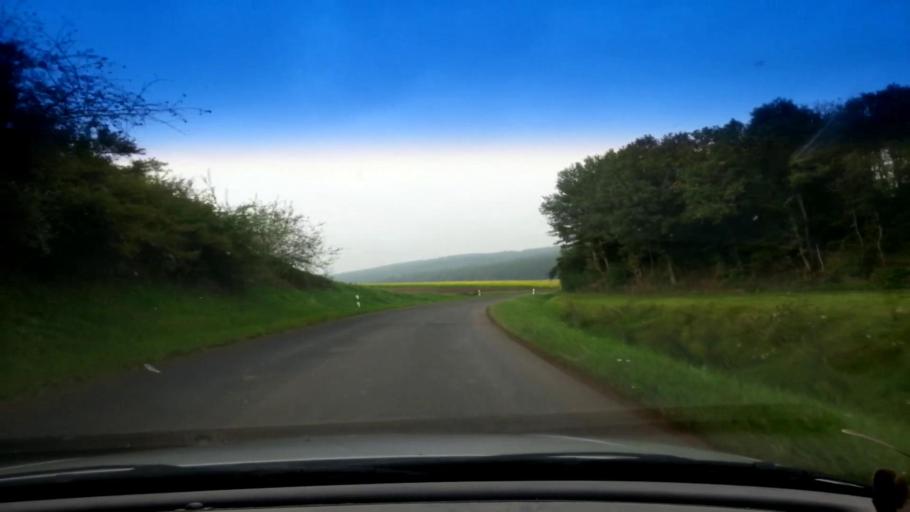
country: DE
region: Bavaria
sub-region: Upper Franconia
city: Rattelsdorf
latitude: 50.0526
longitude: 10.8871
